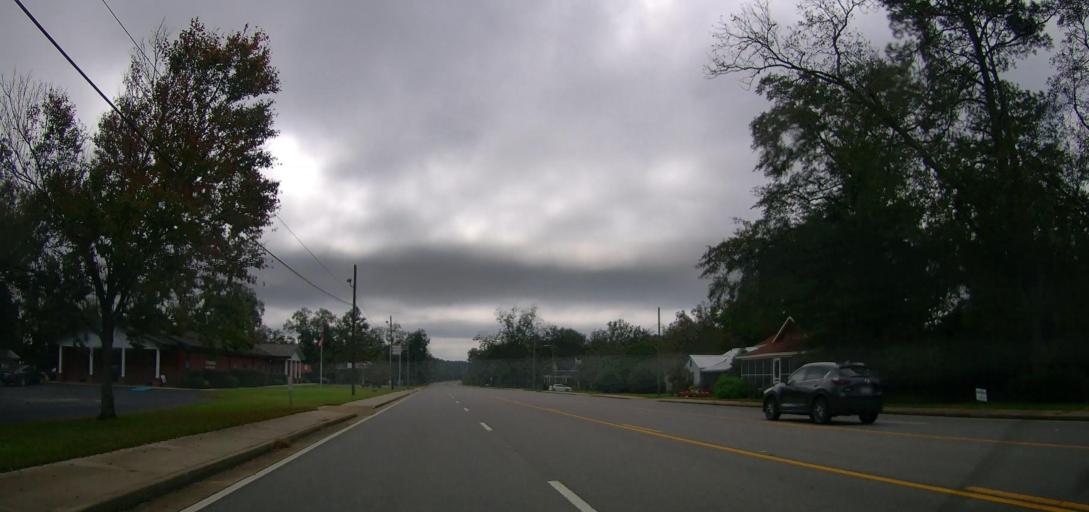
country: US
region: Georgia
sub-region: Colquitt County
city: Moultrie
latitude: 31.0087
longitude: -83.8673
